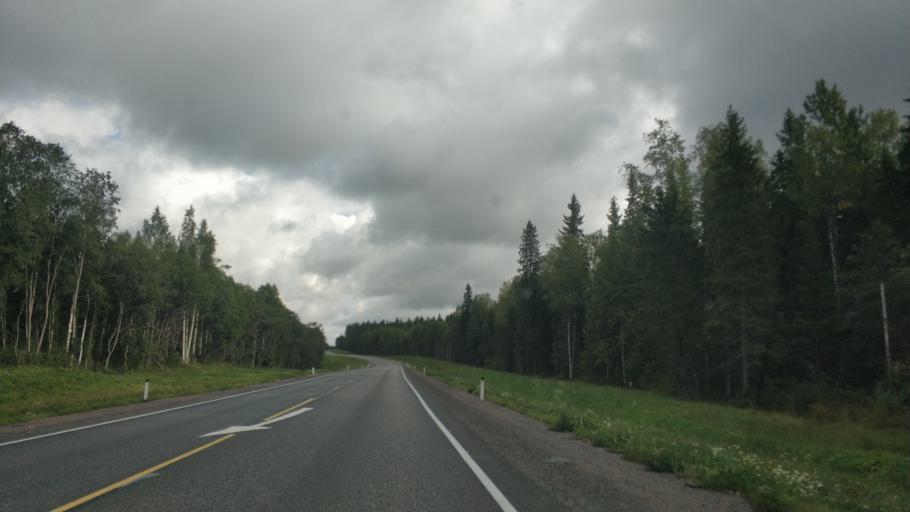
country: RU
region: Republic of Karelia
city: Ruskeala
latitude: 61.8534
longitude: 30.6509
